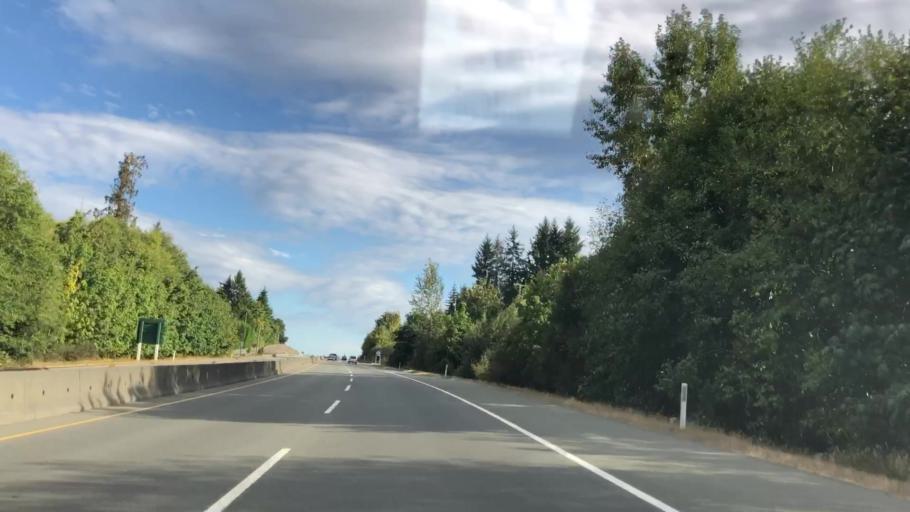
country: CA
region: British Columbia
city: North Saanich
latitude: 48.6477
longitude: -123.5586
